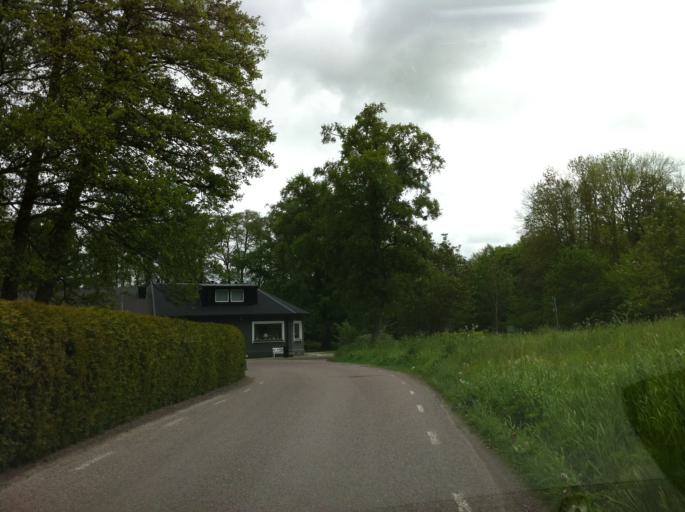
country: SE
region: Skane
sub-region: Kavlinge Kommun
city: Kaevlinge
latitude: 55.8151
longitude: 13.0611
